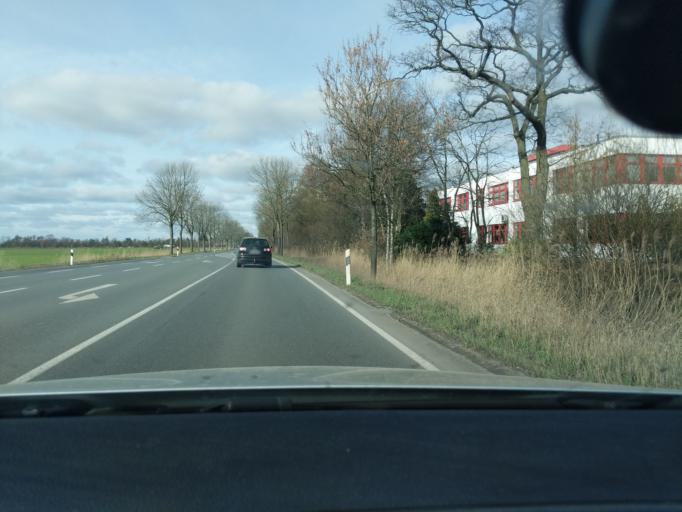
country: DE
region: Lower Saxony
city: Stade
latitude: 53.6199
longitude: 9.4943
